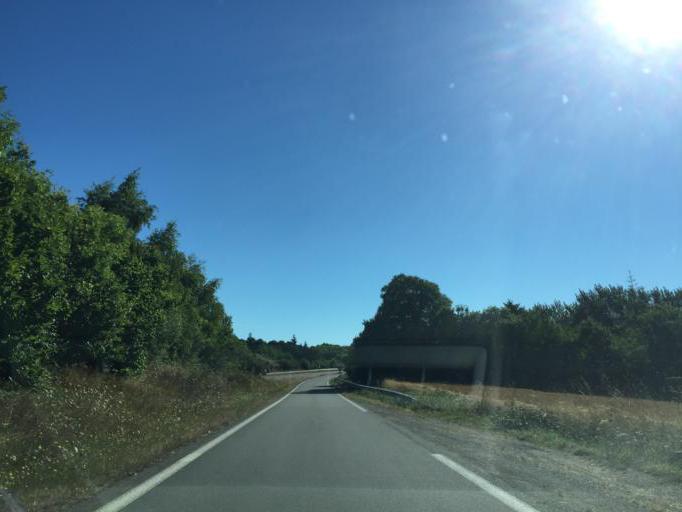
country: FR
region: Brittany
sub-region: Departement des Cotes-d'Armor
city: Jugon-les-Lacs
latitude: 48.4160
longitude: -2.3153
